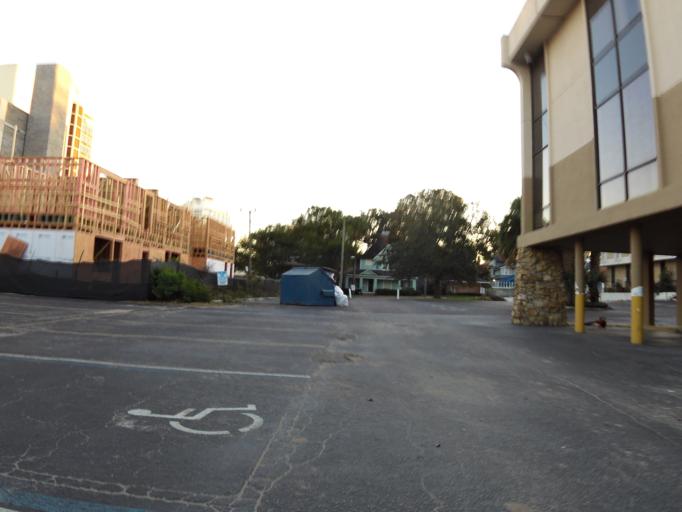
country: US
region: Florida
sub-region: Duval County
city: Jacksonville
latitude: 30.3131
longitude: -81.6773
